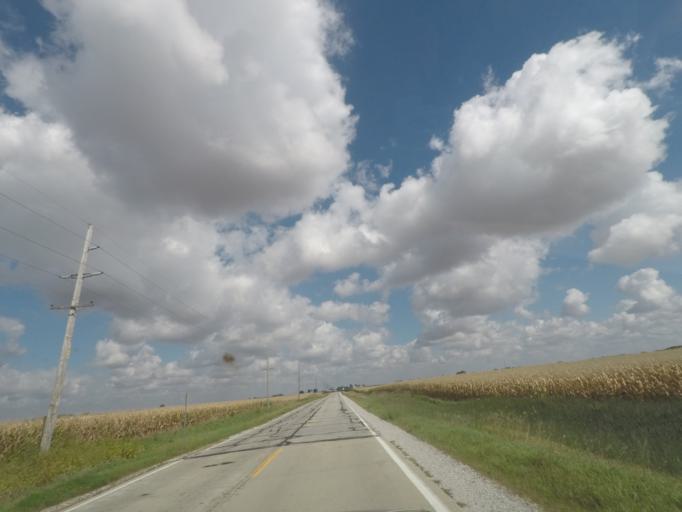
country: US
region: Iowa
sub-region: Story County
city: Nevada
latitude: 42.0101
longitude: -93.4058
